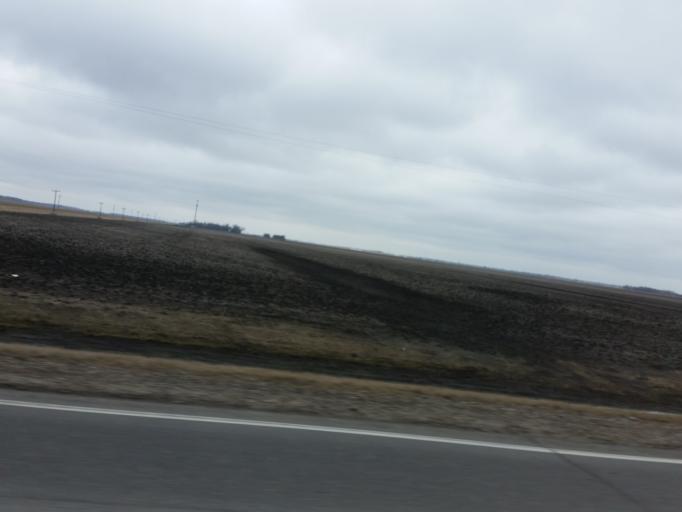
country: US
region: North Dakota
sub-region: Cass County
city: Horace
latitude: 46.6302
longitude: -96.8416
